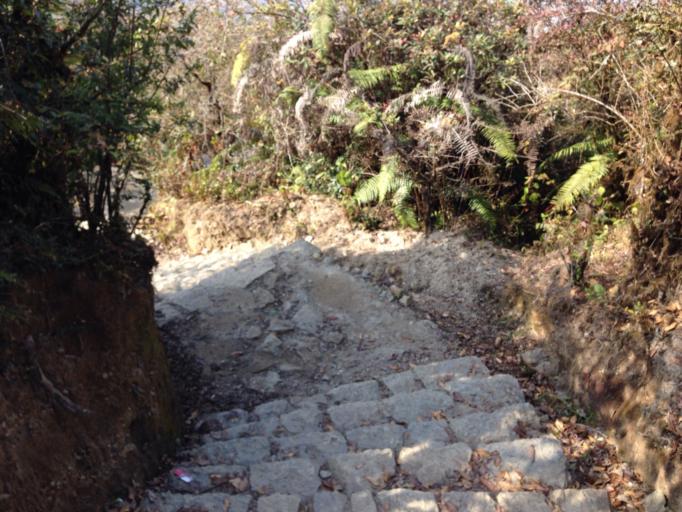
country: NP
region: Central Region
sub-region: Bagmati Zone
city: Nagarkot
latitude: 27.8193
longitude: 85.4473
